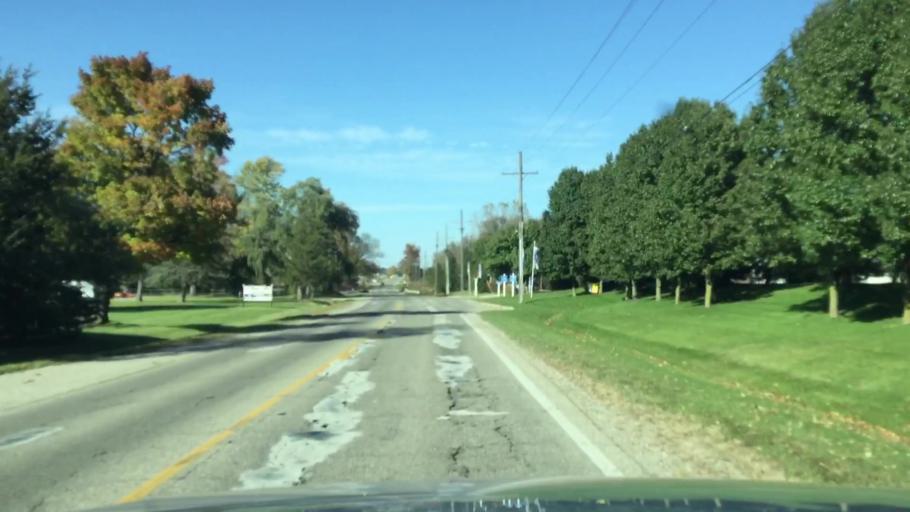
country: US
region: Michigan
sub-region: Lapeer County
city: Lapeer
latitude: 43.0766
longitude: -83.3066
